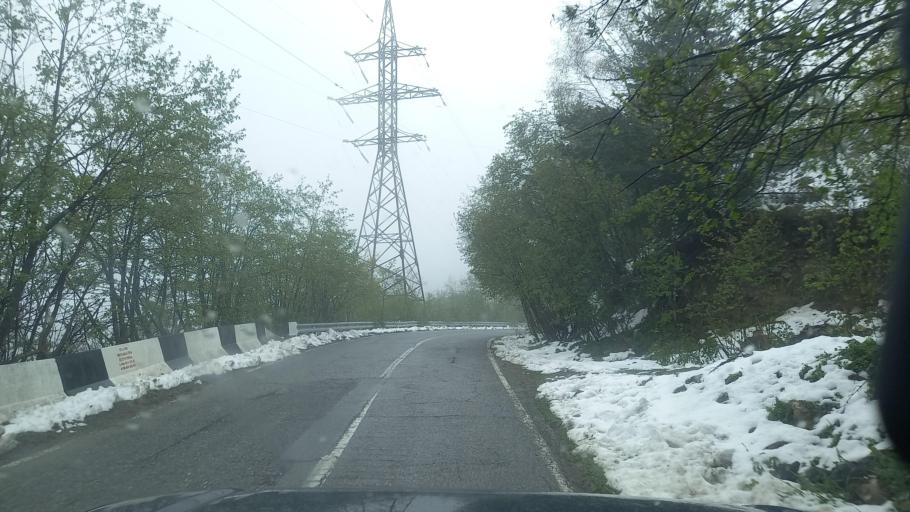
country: RU
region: North Ossetia
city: Mizur
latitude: 42.7992
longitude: 43.9326
